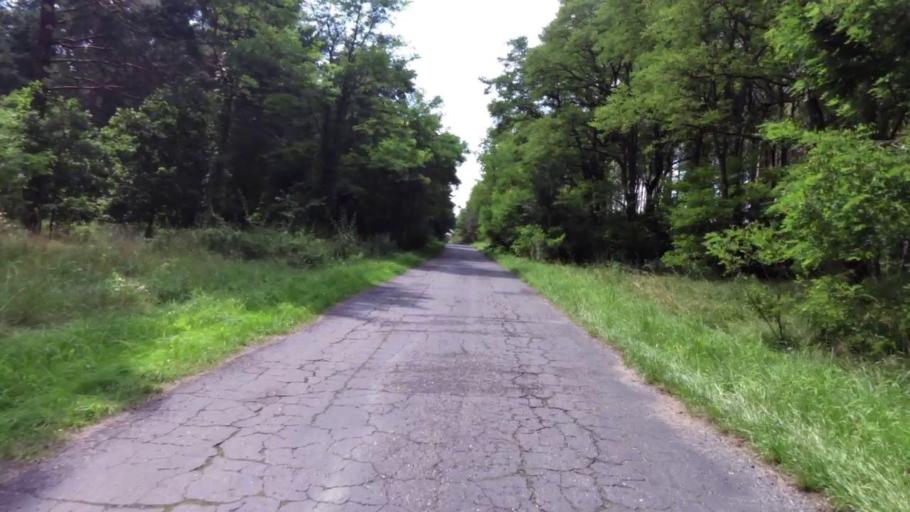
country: PL
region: West Pomeranian Voivodeship
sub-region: Powiat stargardzki
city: Dobrzany
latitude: 53.3780
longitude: 15.3745
